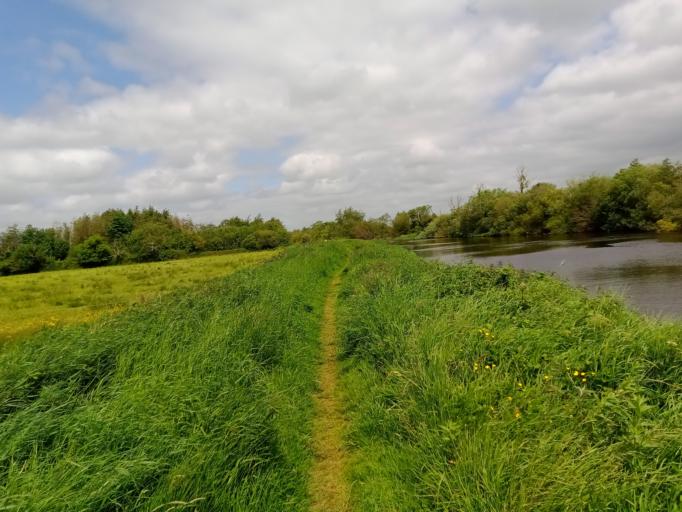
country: IE
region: Leinster
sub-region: County Carlow
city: Carlow
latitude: 52.7926
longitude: -6.9606
